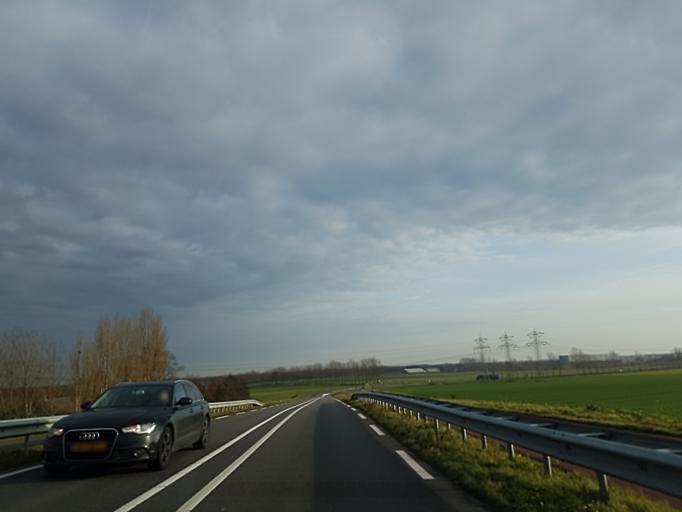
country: NL
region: North Brabant
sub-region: Roosendaal
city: Roosendaal
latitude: 51.5585
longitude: 4.4841
